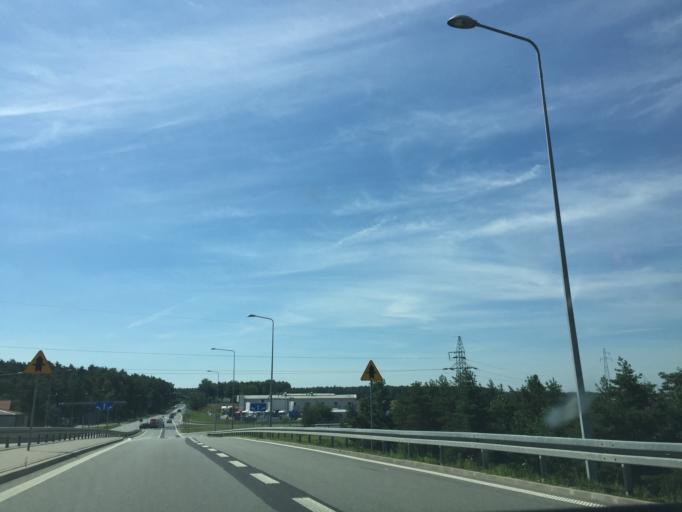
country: PL
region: Lodz Voivodeship
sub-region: Piotrkow Trybunalski
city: Piotrkow Trybunalski
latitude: 51.4430
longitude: 19.7229
